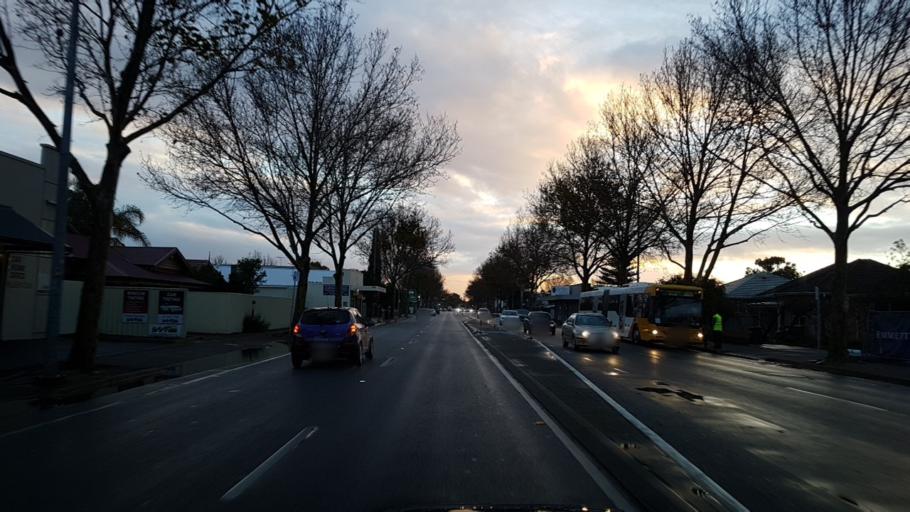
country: AU
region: South Australia
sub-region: City of West Torrens
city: Plympton
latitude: -34.9326
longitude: 138.5565
